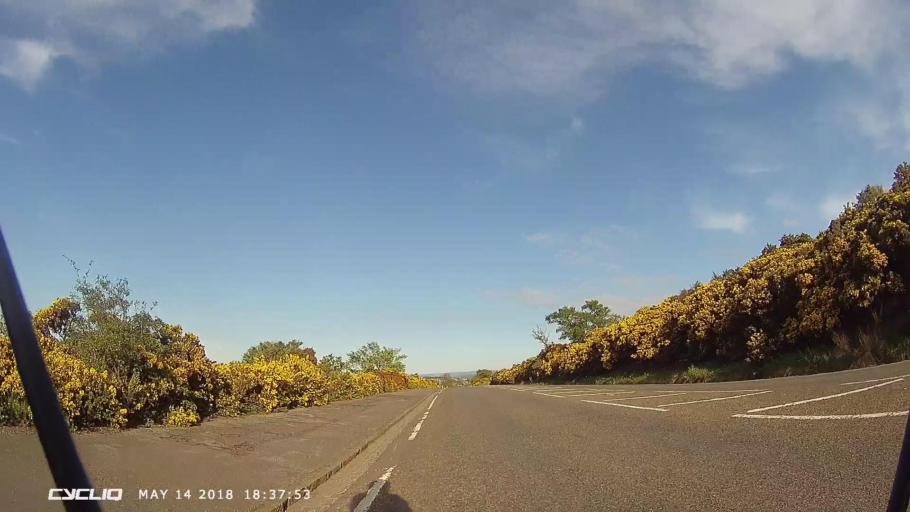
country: GB
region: Scotland
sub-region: Edinburgh
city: Edinburgh
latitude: 55.9170
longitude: -3.1912
